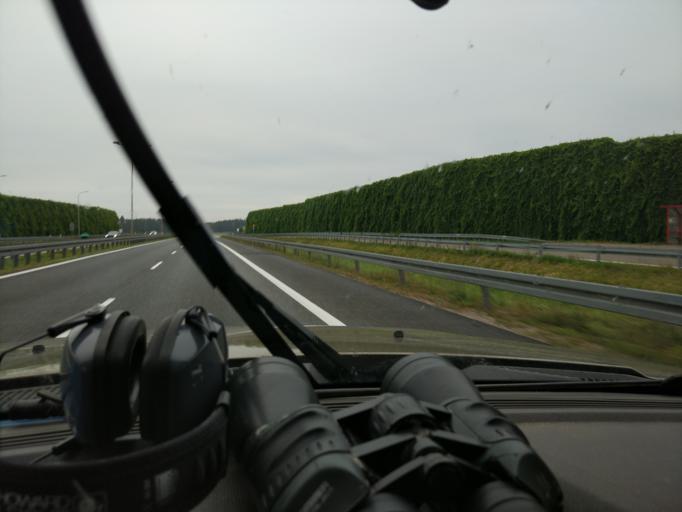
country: PL
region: Masovian Voivodeship
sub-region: Powiat wolominski
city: Dabrowka
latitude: 52.4933
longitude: 21.3672
